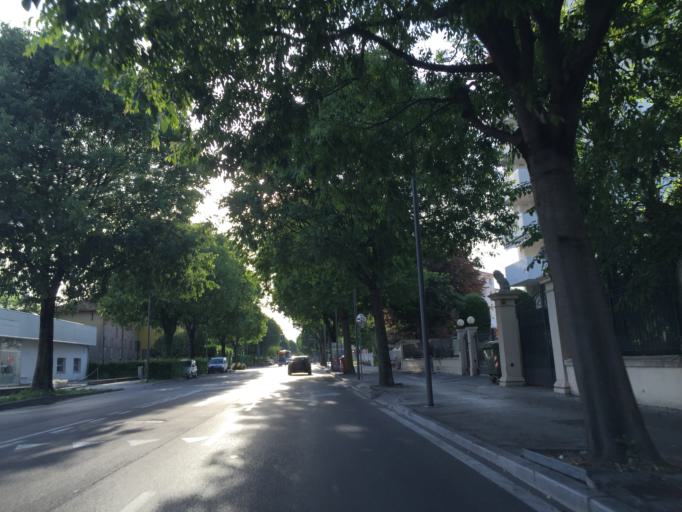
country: IT
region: Friuli Venezia Giulia
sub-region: Provincia di Pordenone
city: Pordenone
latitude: 45.9640
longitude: 12.6487
